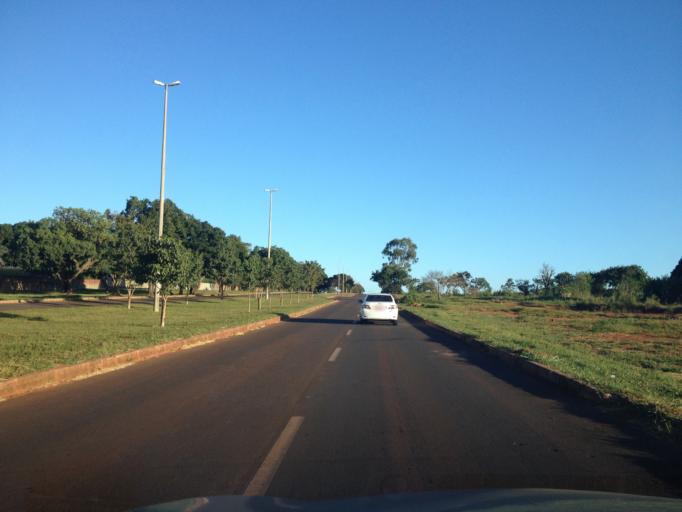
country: BR
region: Federal District
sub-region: Brasilia
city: Brasilia
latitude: -15.7601
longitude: -47.8995
